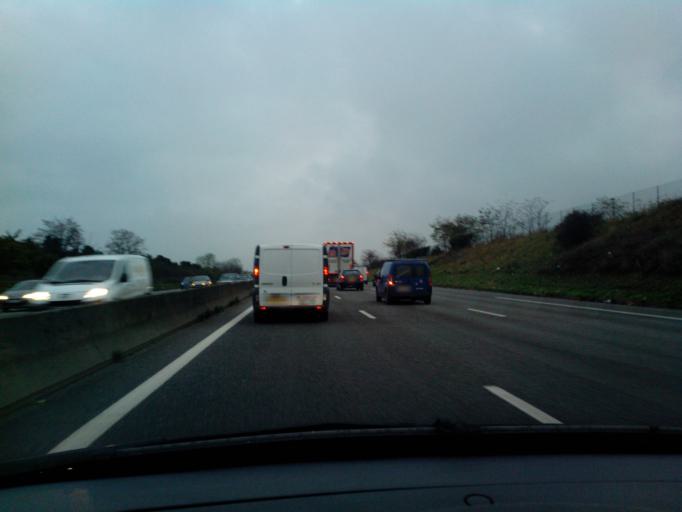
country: FR
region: Ile-de-France
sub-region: Departement de l'Essonne
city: Chilly-Mazarin
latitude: 48.7226
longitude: 2.3119
